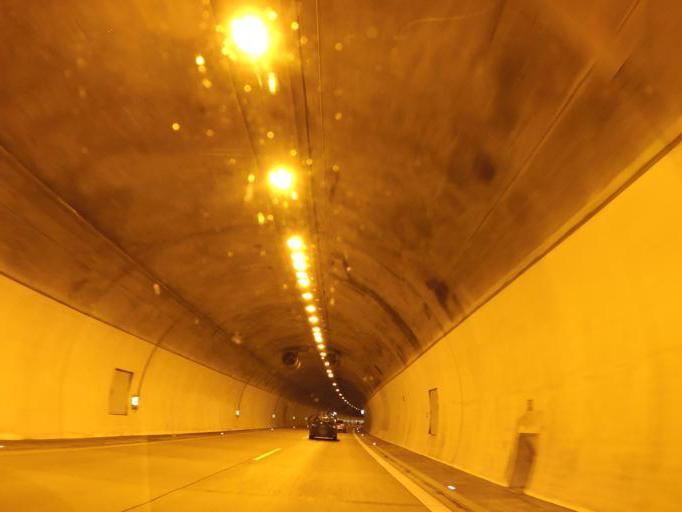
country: DE
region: Baden-Wuerttemberg
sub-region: Regierungsbezirk Stuttgart
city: Westhausen
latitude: 48.8721
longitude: 10.1697
